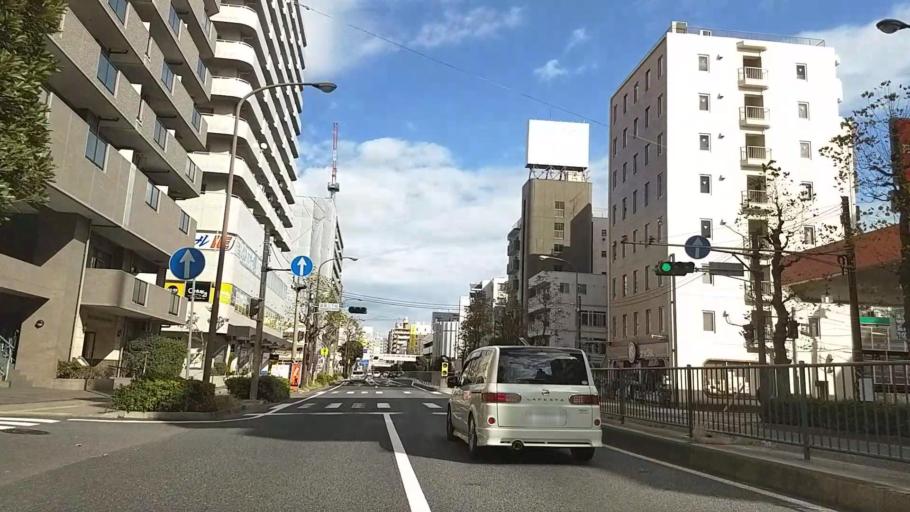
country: JP
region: Kanagawa
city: Yokohama
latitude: 35.4764
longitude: 139.6276
